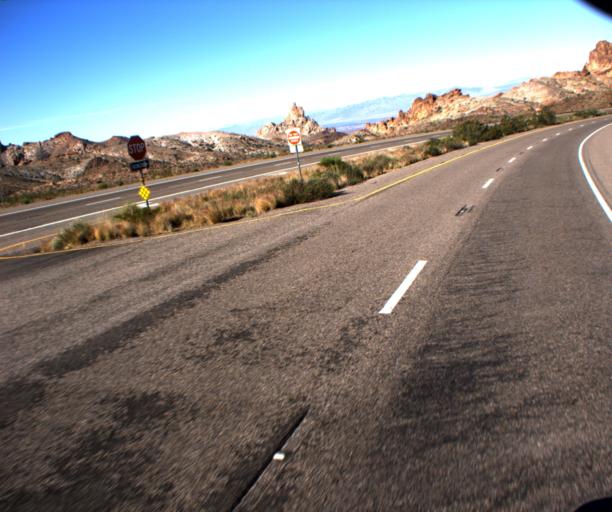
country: US
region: Arizona
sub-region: Mohave County
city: Bullhead City
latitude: 35.1945
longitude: -114.4077
